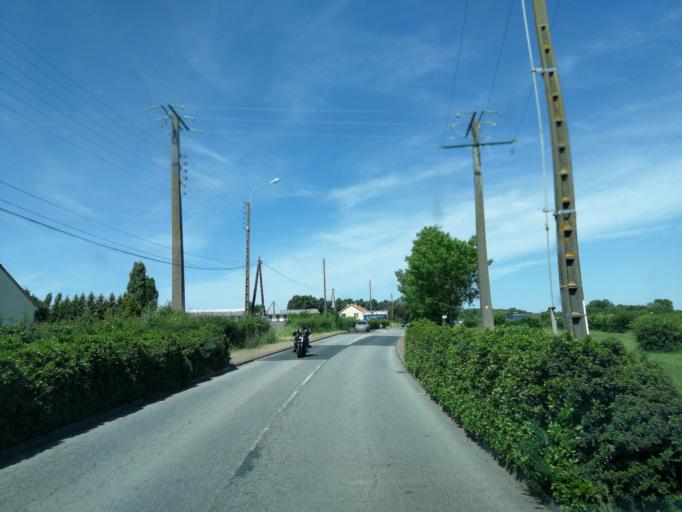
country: FR
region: Poitou-Charentes
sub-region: Departement des Deux-Sevres
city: Saint-Varent
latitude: 46.9028
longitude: -0.2874
